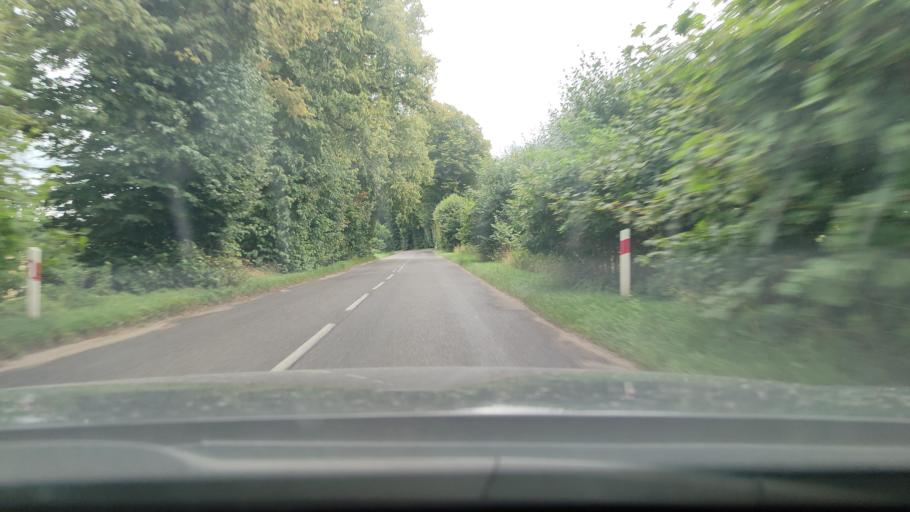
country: PL
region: Pomeranian Voivodeship
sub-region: Powiat pucki
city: Krokowa
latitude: 54.7701
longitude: 18.1630
